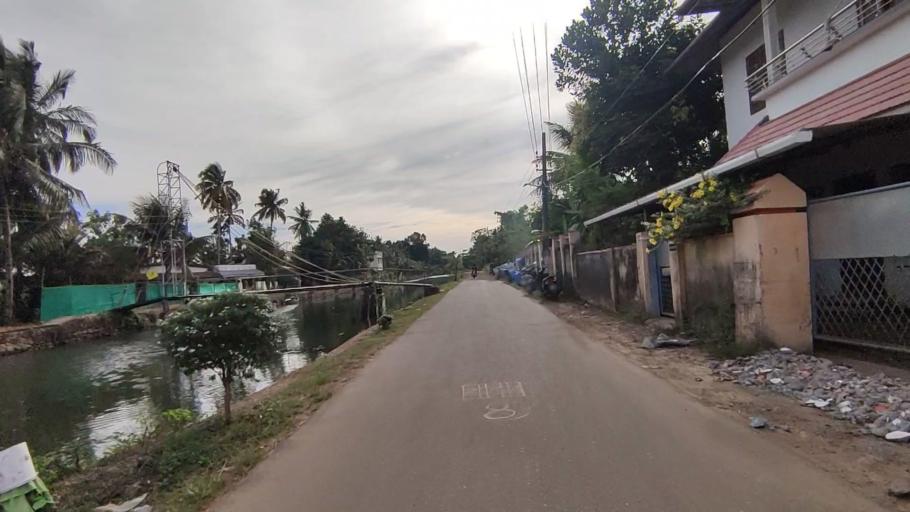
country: IN
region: Kerala
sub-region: Kottayam
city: Kottayam
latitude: 9.5717
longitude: 76.4984
